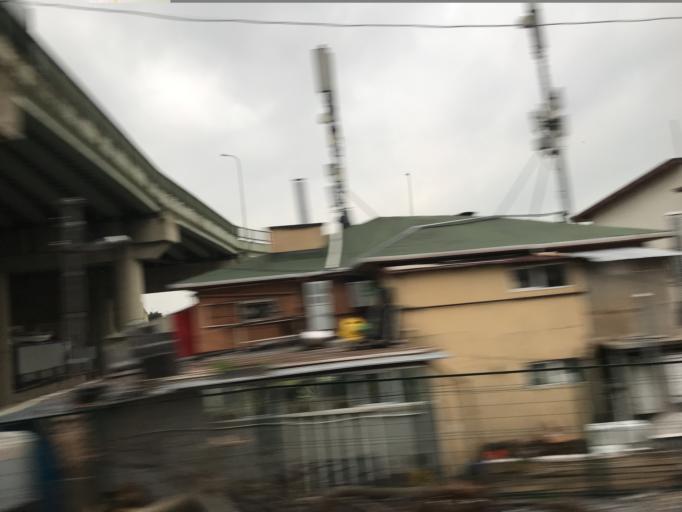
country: TR
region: Istanbul
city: Maltepe
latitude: 40.9341
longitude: 29.1172
